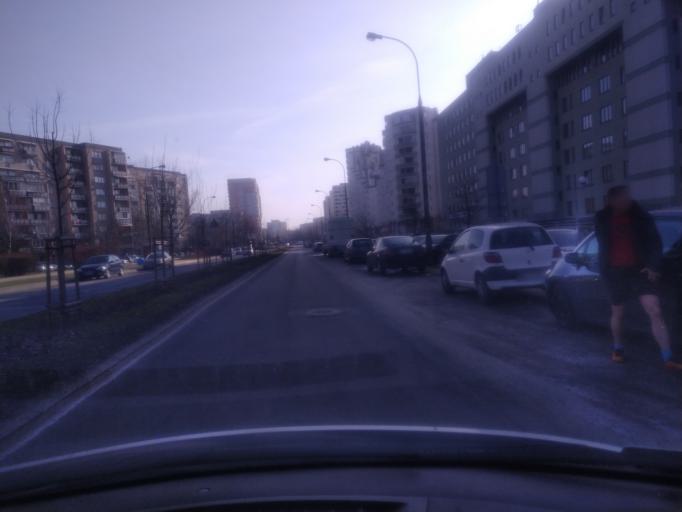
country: PL
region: Masovian Voivodeship
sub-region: Warszawa
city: Praga Poludnie
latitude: 52.2229
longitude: 21.0860
